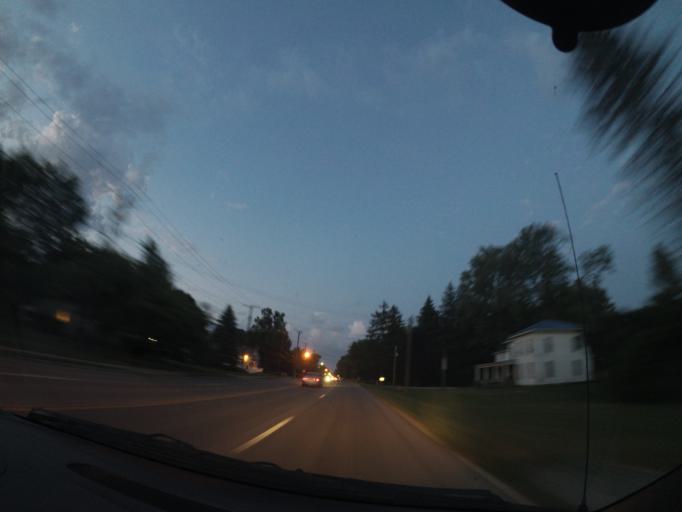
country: US
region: Ohio
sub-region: Ashtabula County
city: Geneva
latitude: 41.8105
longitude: -80.9292
